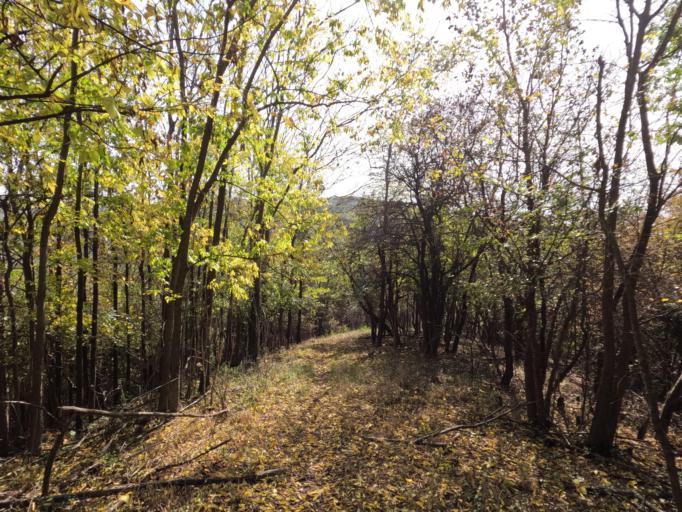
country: HU
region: Tolna
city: Szentgalpuszta
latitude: 46.3443
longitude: 18.6288
